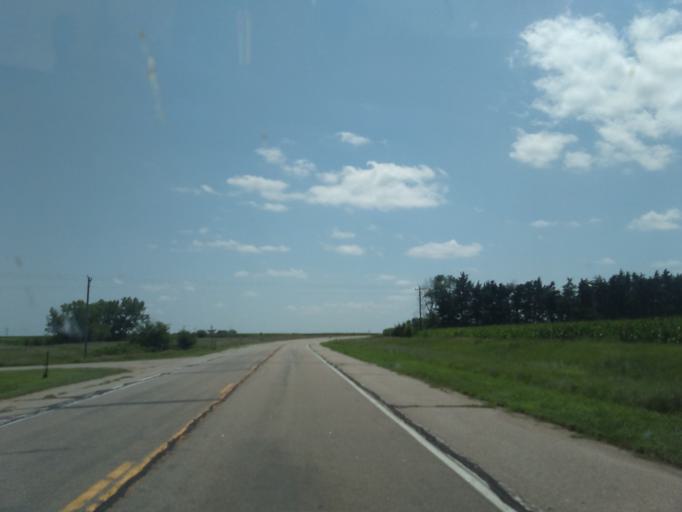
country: US
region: Nebraska
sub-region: Dawson County
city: Lexington
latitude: 40.6910
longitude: -99.7947
